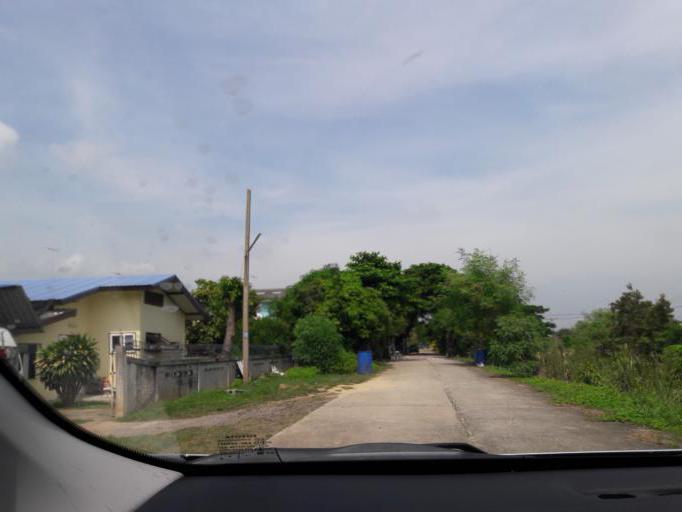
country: TH
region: Ang Thong
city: Ang Thong
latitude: 14.5740
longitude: 100.4548
